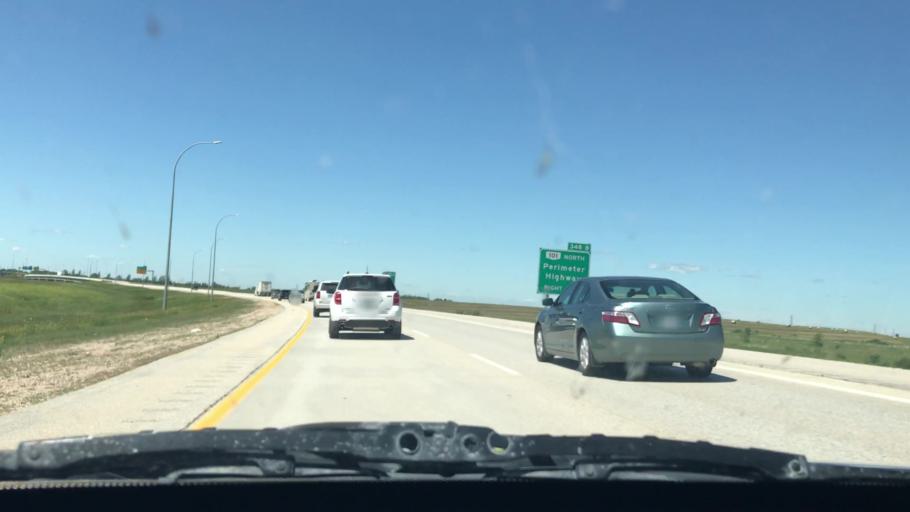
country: CA
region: Manitoba
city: Winnipeg
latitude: 49.8280
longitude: -96.9476
